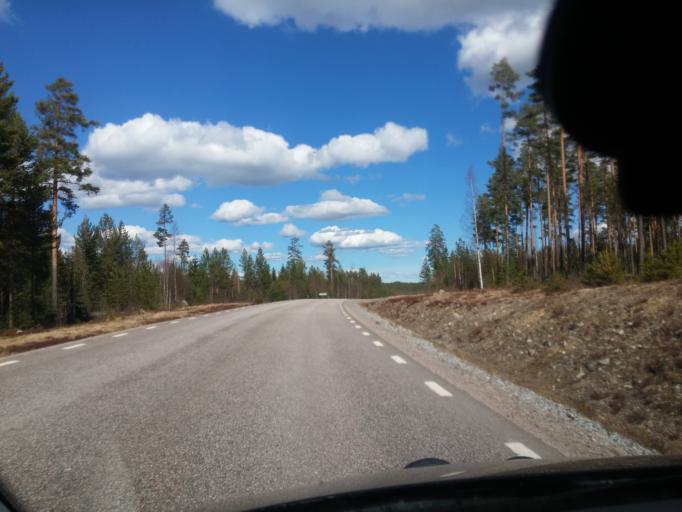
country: SE
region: Gaevleborg
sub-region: Ovanakers Kommun
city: Edsbyn
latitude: 61.2783
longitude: 15.8968
